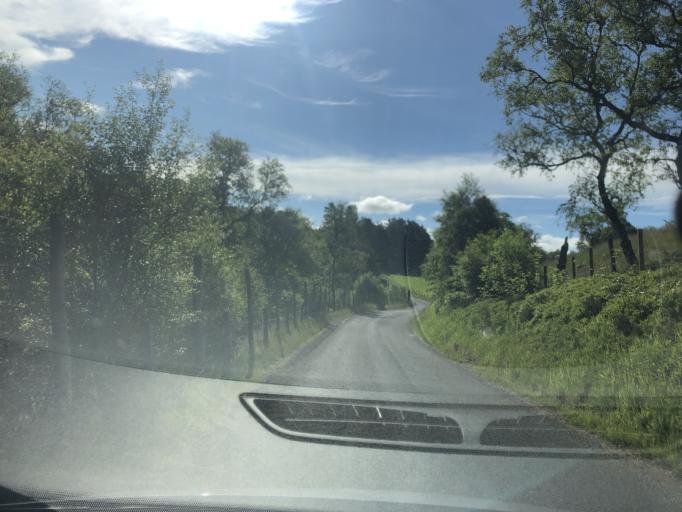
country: GB
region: Scotland
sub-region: Angus
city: Kirriemuir
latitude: 56.8374
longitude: -3.0858
